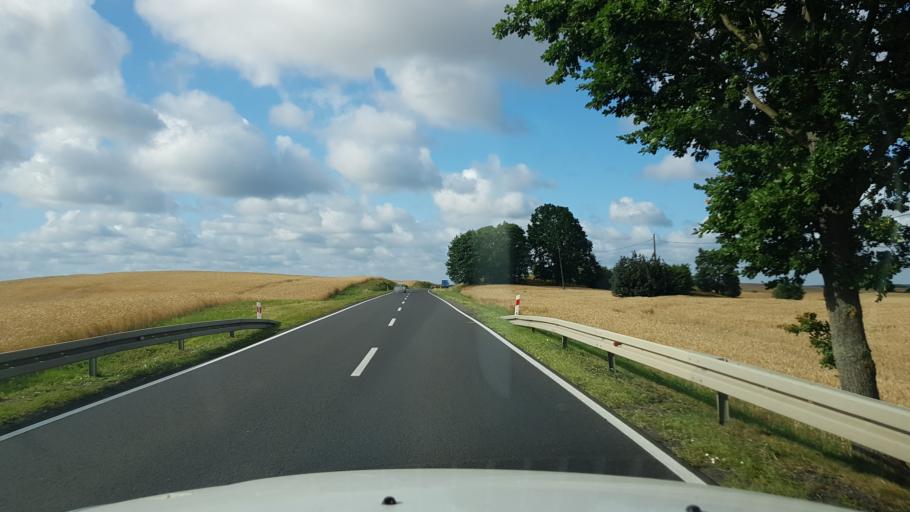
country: PL
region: West Pomeranian Voivodeship
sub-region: Powiat mysliborski
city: Mysliborz
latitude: 52.8976
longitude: 14.8511
